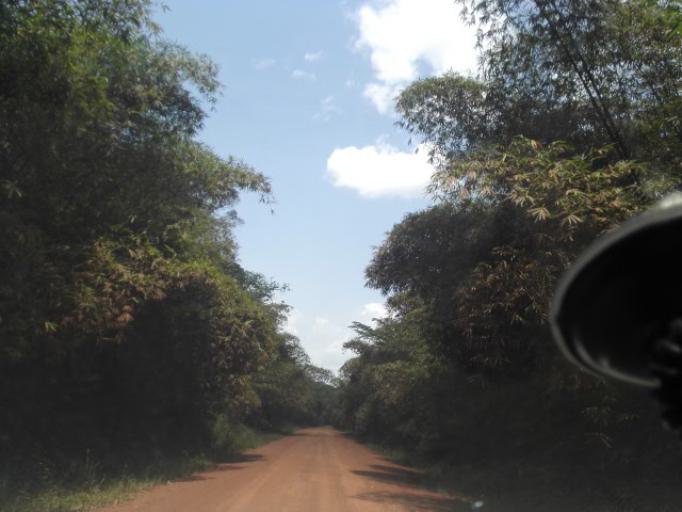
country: CD
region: Eastern Province
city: Kisangani
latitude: 0.6265
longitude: 26.0612
